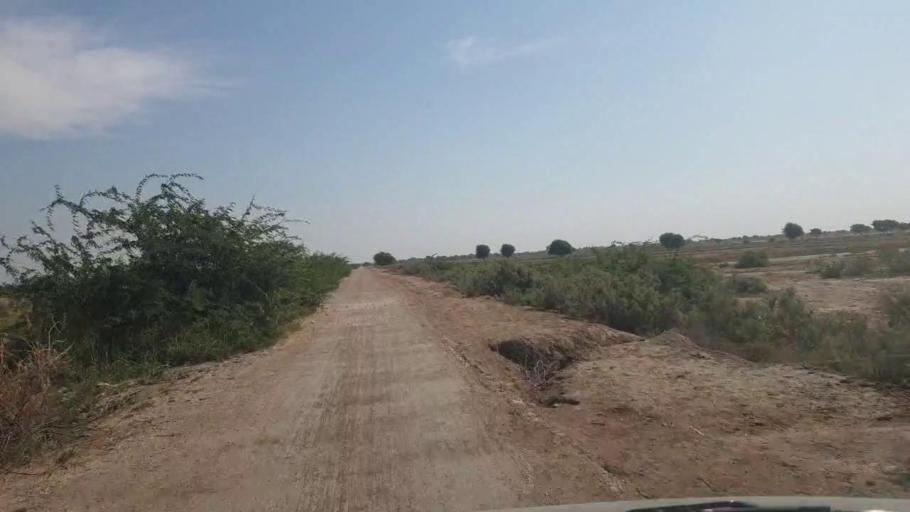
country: PK
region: Sindh
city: Digri
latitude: 24.9634
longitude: 69.1233
